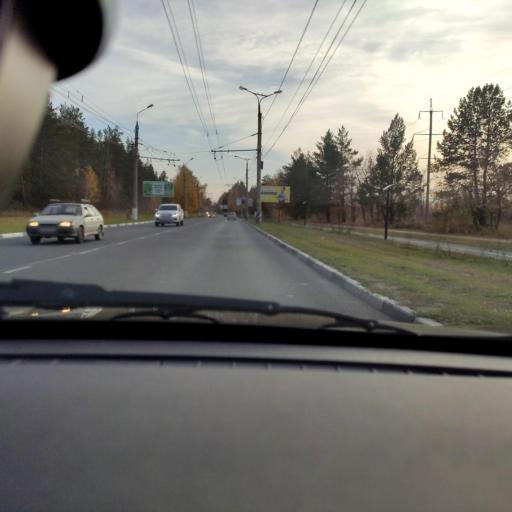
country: RU
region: Samara
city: Tol'yatti
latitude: 53.4958
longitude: 49.3875
